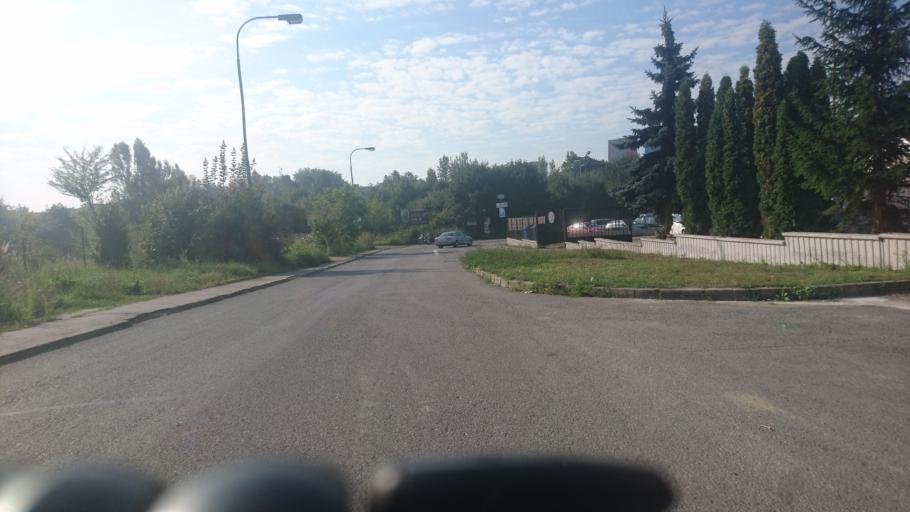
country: CZ
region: South Moravian
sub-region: Mesto Brno
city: Mokra Hora
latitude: 49.2338
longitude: 16.5842
